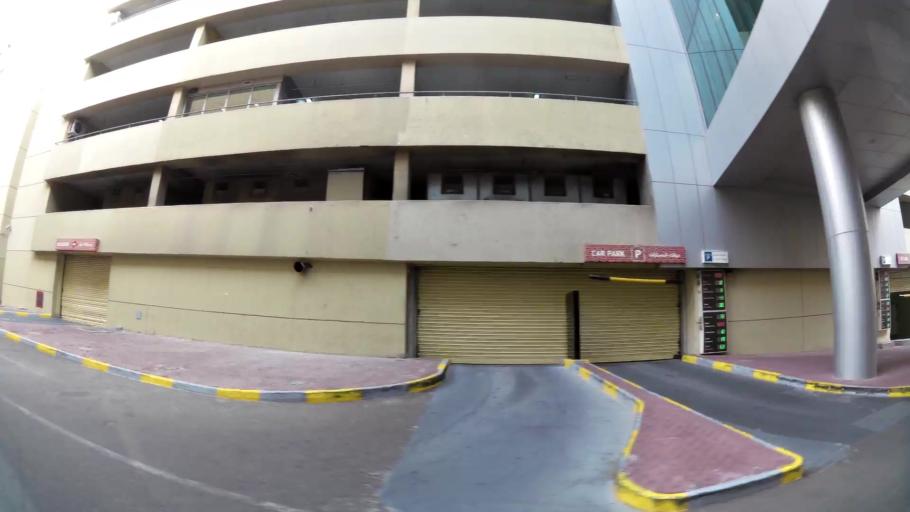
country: AE
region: Abu Dhabi
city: Abu Dhabi
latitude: 24.4703
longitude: 54.3741
